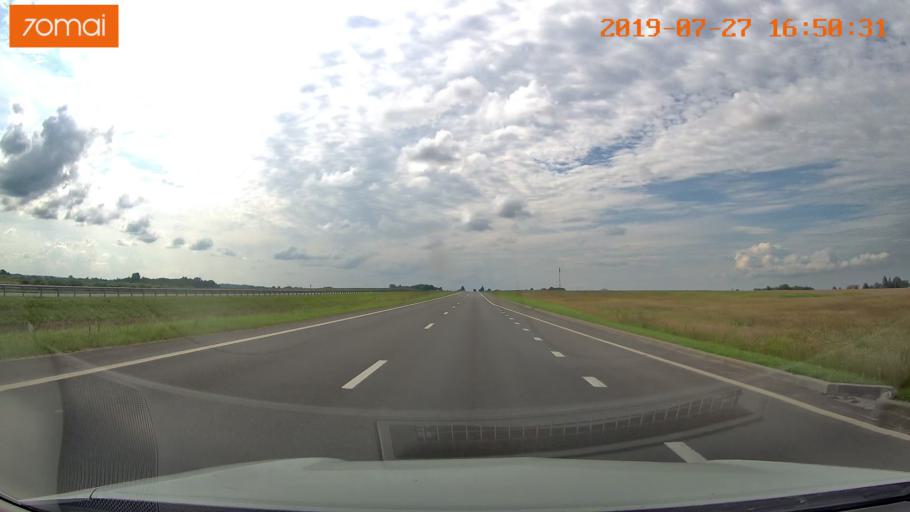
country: RU
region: Kaliningrad
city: Gvardeysk
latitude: 54.6780
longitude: 20.9113
